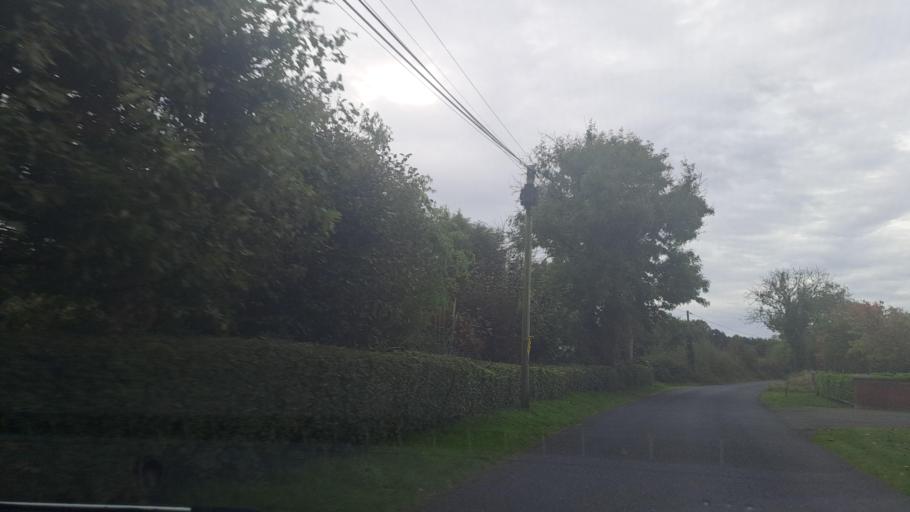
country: IE
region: Ulster
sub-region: County Monaghan
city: Carrickmacross
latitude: 53.9810
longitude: -6.7556
